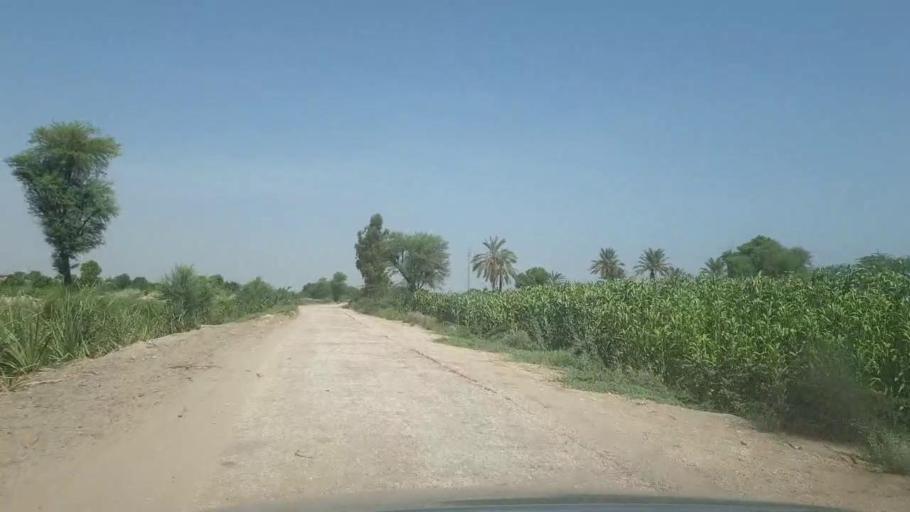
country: PK
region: Sindh
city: Khairpur
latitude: 27.4008
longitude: 69.0385
